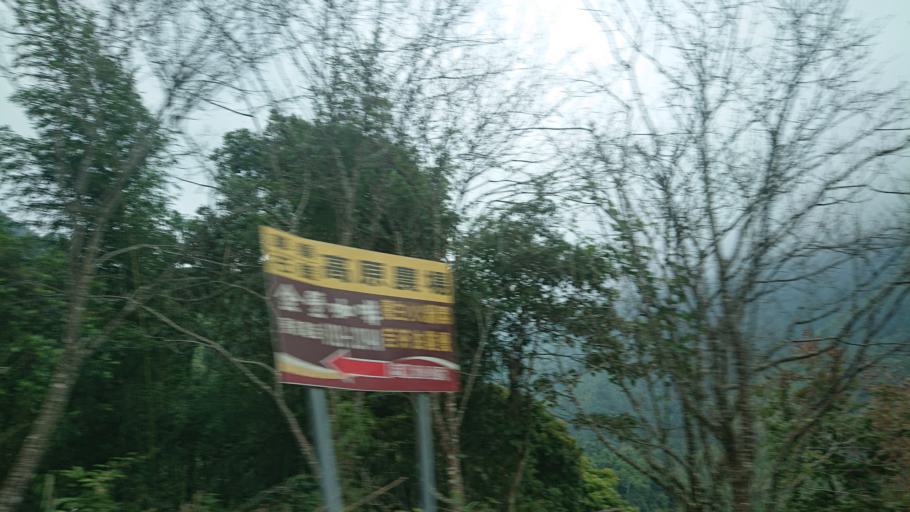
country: TW
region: Taiwan
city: Lugu
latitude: 23.6109
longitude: 120.7138
